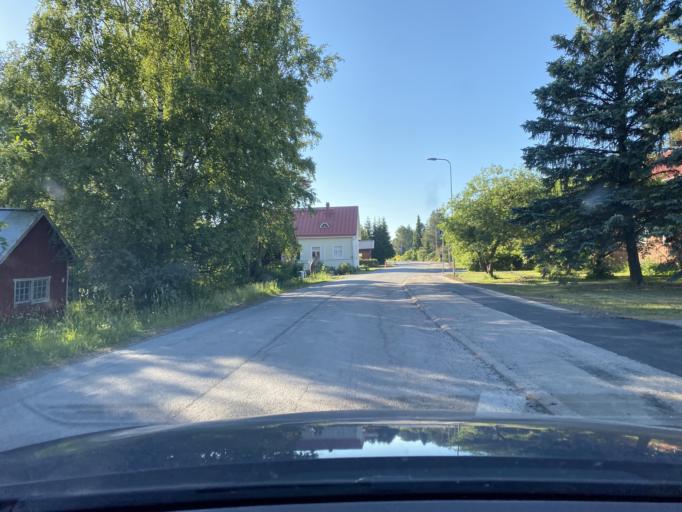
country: FI
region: Satakunta
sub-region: Pori
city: Huittinen
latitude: 61.1704
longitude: 22.6993
